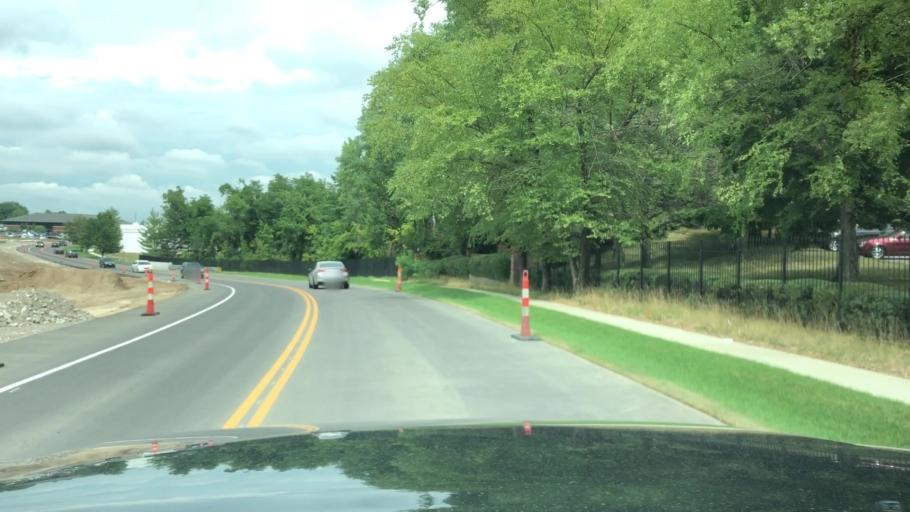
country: US
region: Missouri
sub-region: Saint Charles County
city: Saint Peters
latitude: 38.7988
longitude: -90.5581
